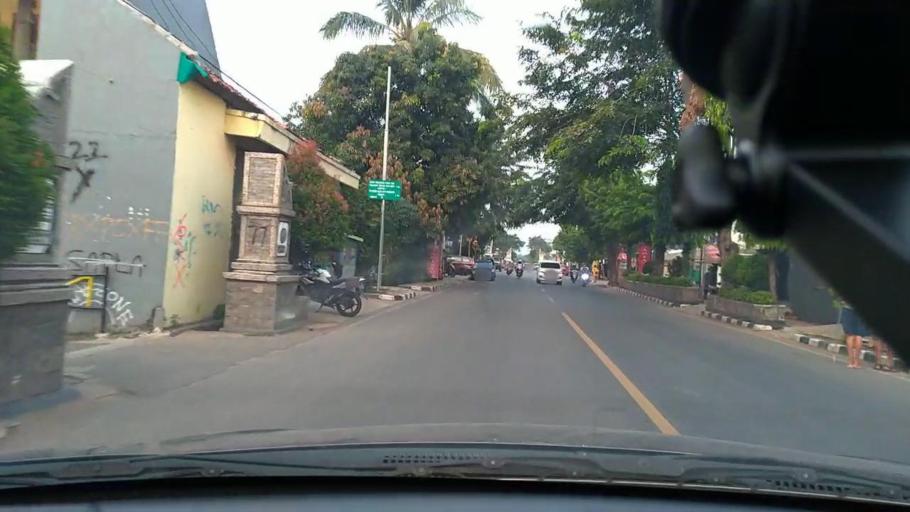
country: ID
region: West Java
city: Purwakarta
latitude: -6.5344
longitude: 107.4435
